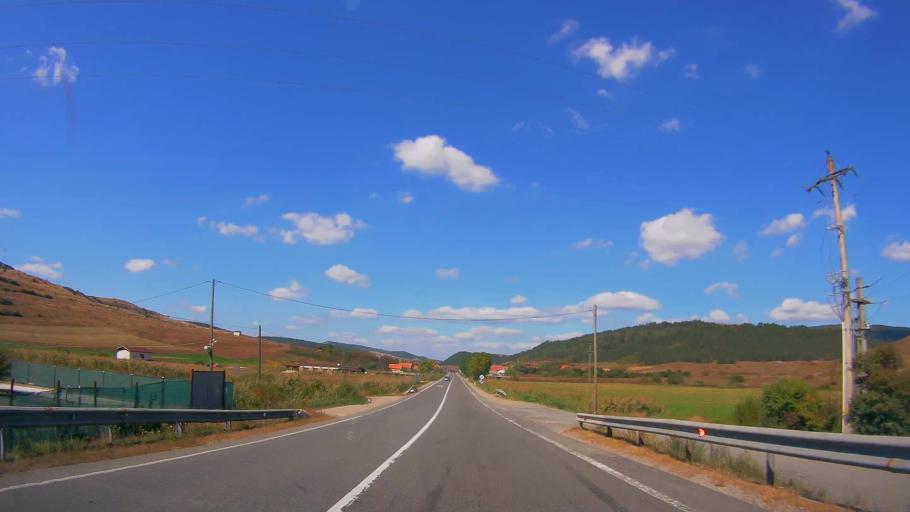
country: RO
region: Cluj
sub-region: Comuna Baciu
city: Mera
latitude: 46.8186
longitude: 23.4232
